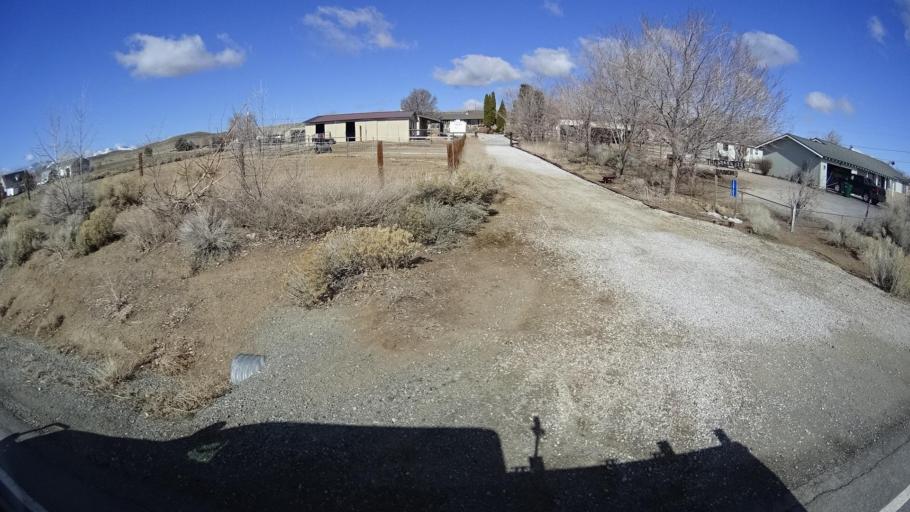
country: US
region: Nevada
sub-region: Washoe County
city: Cold Springs
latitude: 39.6854
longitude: -119.9195
